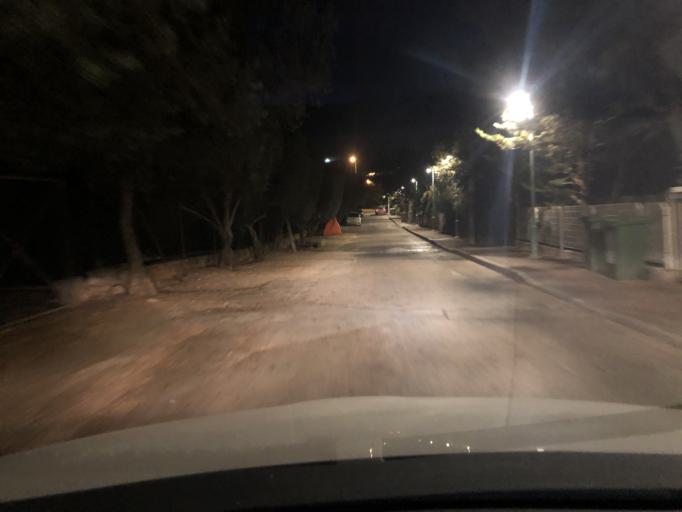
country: IL
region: Central District
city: Hod HaSharon
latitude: 32.1701
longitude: 34.8961
